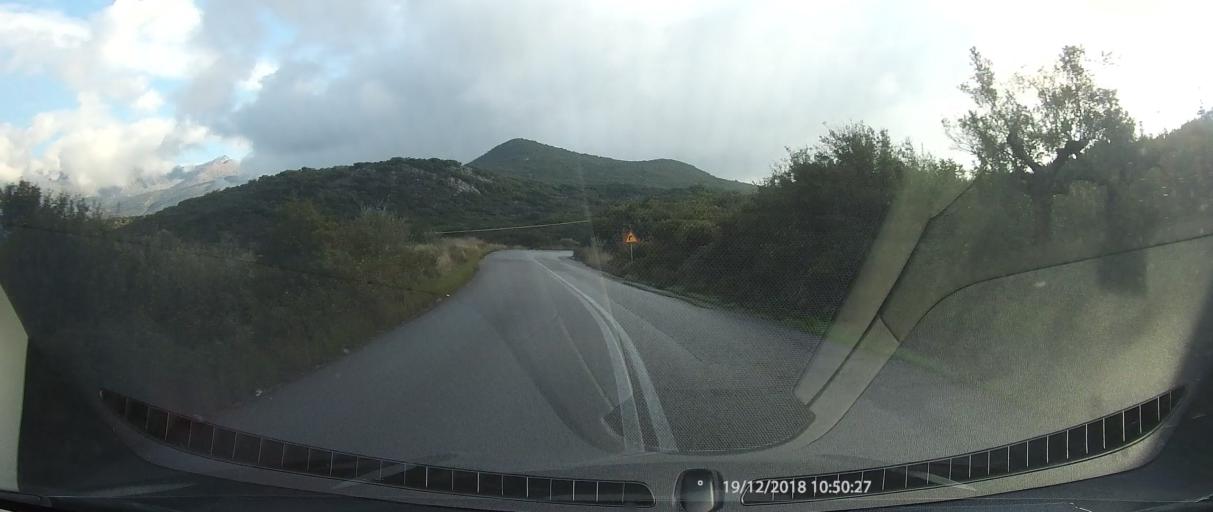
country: GR
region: Peloponnese
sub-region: Nomos Messinias
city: Kardamyli
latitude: 36.9242
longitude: 22.2073
